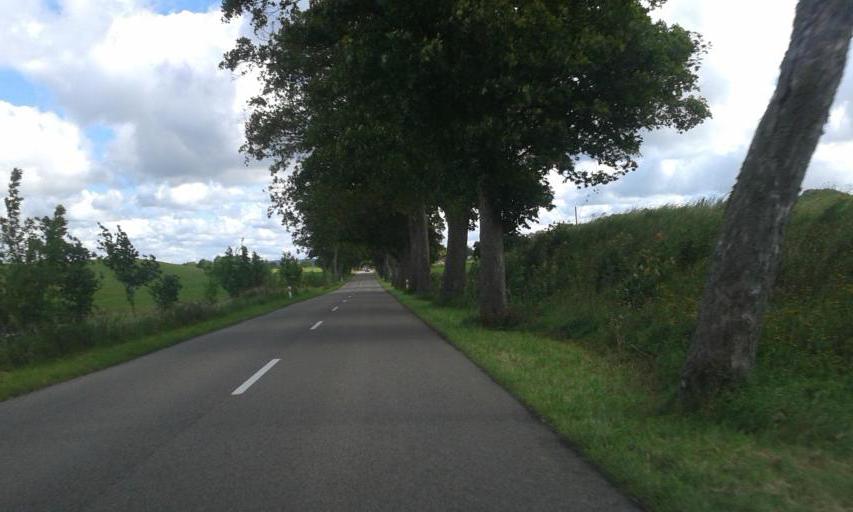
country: PL
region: West Pomeranian Voivodeship
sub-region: Powiat koszalinski
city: Bobolice
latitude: 53.9838
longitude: 16.6774
